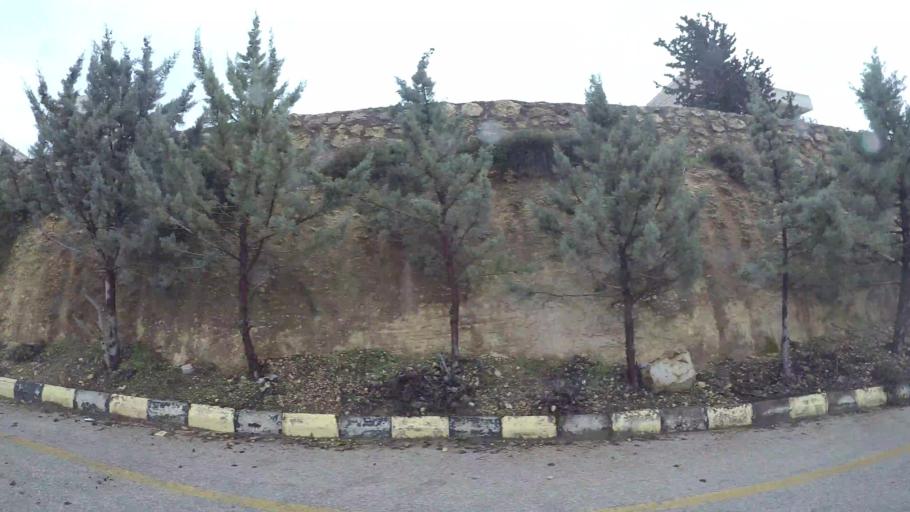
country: JO
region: Amman
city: Al Jubayhah
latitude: 32.0259
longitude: 35.8285
